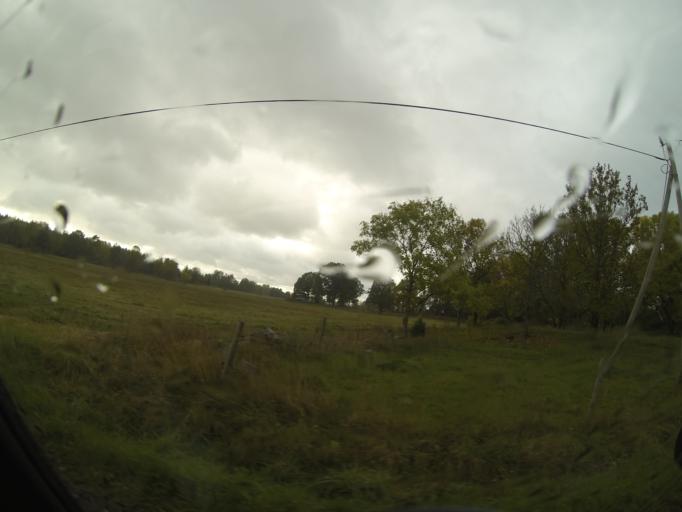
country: SE
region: Soedermanland
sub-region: Eskilstuna Kommun
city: Kvicksund
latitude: 59.3386
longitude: 16.2995
